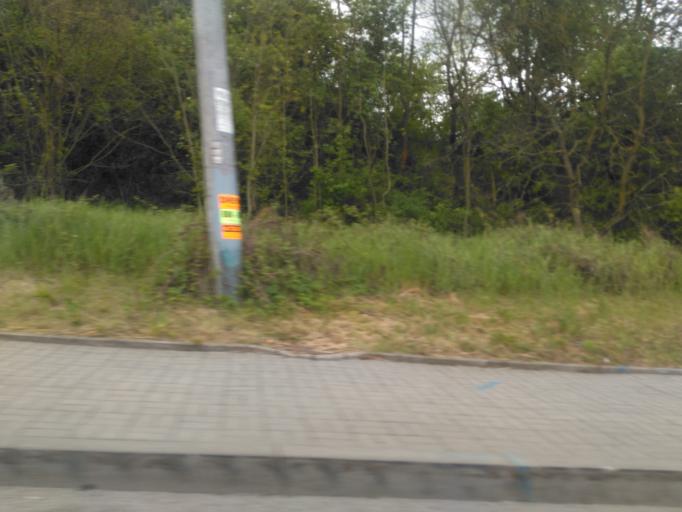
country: CZ
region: Central Bohemia
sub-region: Okres Beroun
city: Beroun
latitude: 49.9702
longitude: 14.0823
